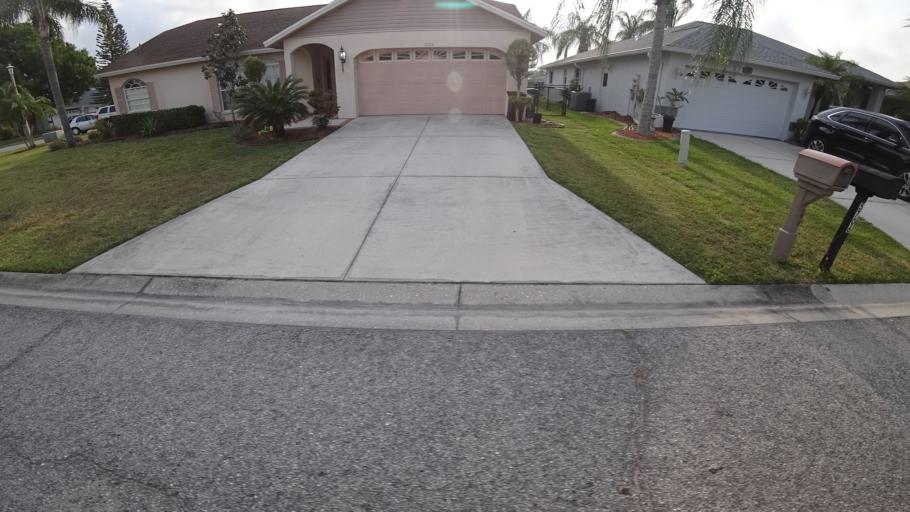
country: US
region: Florida
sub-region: Manatee County
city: Samoset
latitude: 27.4391
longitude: -82.5293
